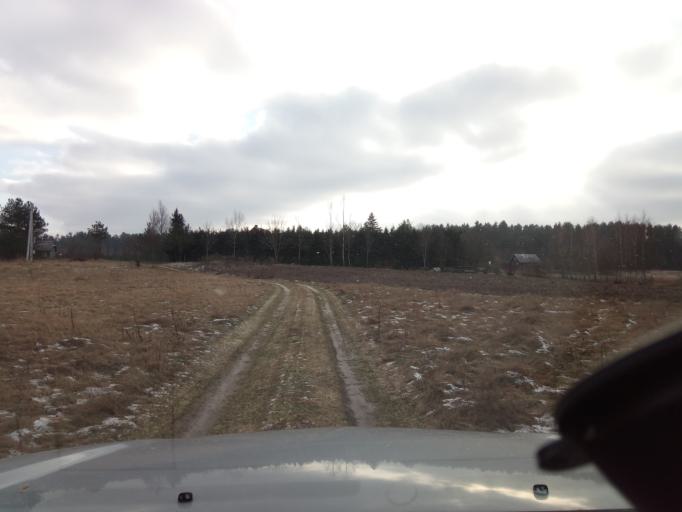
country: LT
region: Alytaus apskritis
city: Druskininkai
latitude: 54.1129
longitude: 24.2193
